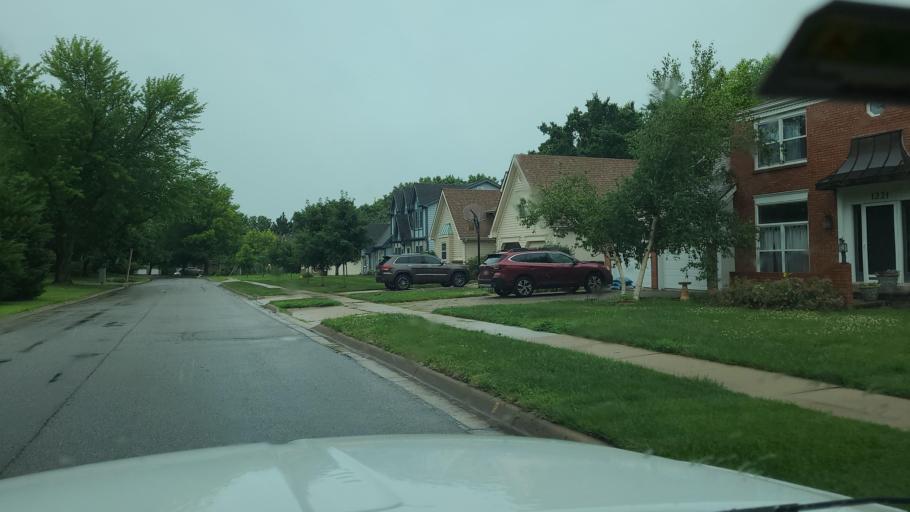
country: US
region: Kansas
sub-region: Douglas County
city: Lawrence
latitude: 38.9610
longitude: -95.2971
